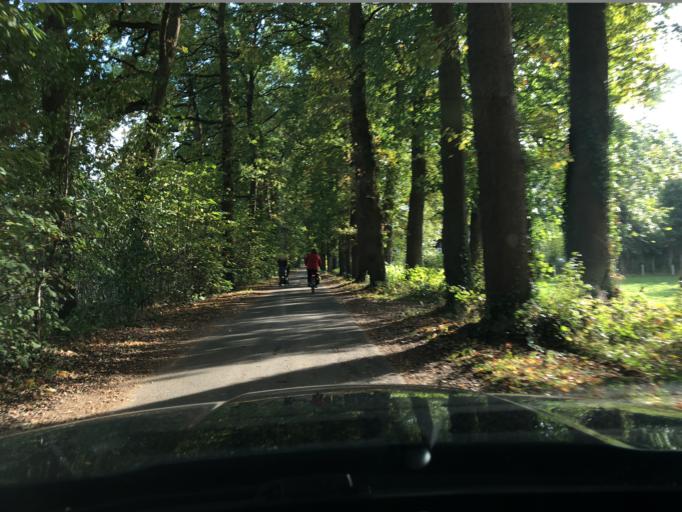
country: DE
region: North Rhine-Westphalia
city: Lengerich
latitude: 52.1716
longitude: 7.8413
